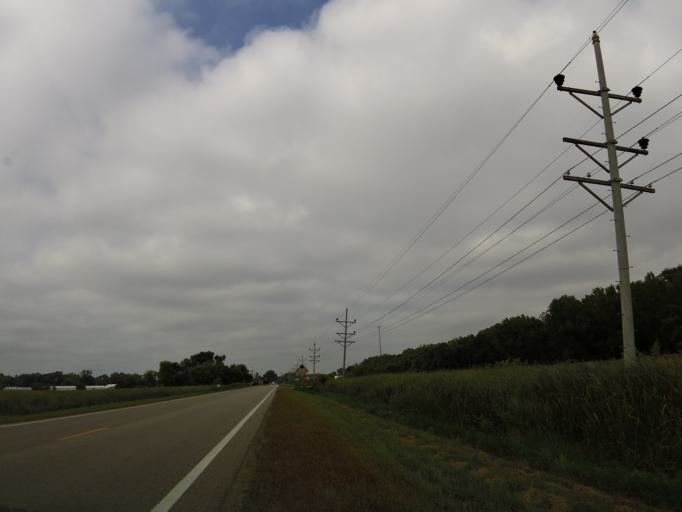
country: US
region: Minnesota
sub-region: Chippewa County
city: Montevideo
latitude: 44.9352
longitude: -95.7164
